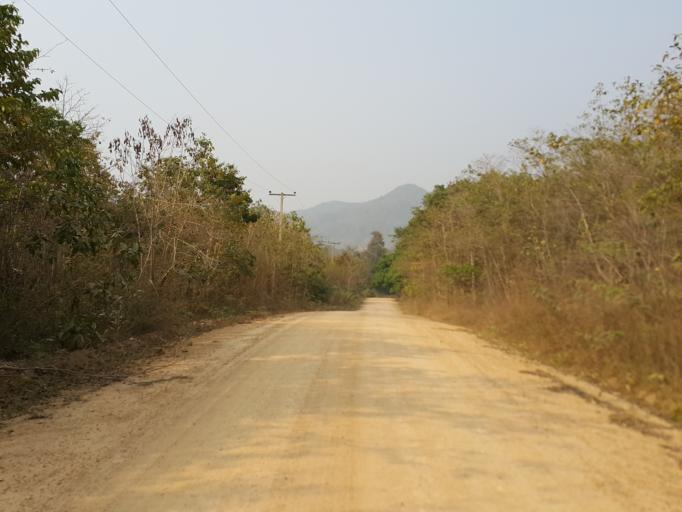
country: TH
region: Lampang
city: Mae Phrik
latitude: 17.5963
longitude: 98.9731
